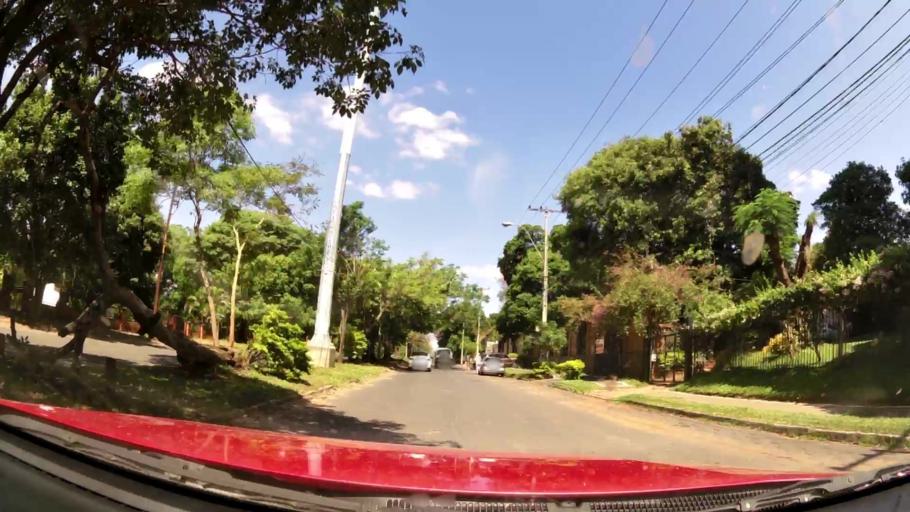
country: PY
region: Asuncion
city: Asuncion
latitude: -25.2603
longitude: -57.5637
